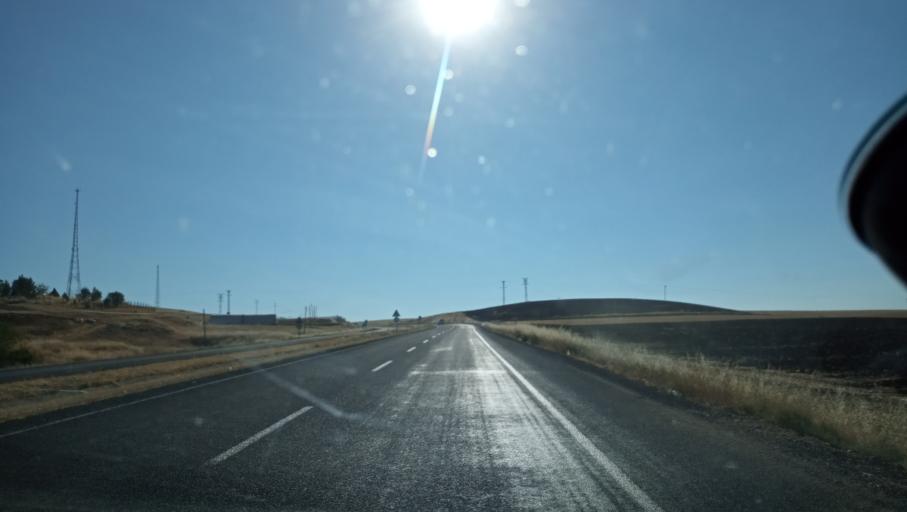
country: TR
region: Diyarbakir
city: Sur
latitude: 37.9914
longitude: 40.3911
